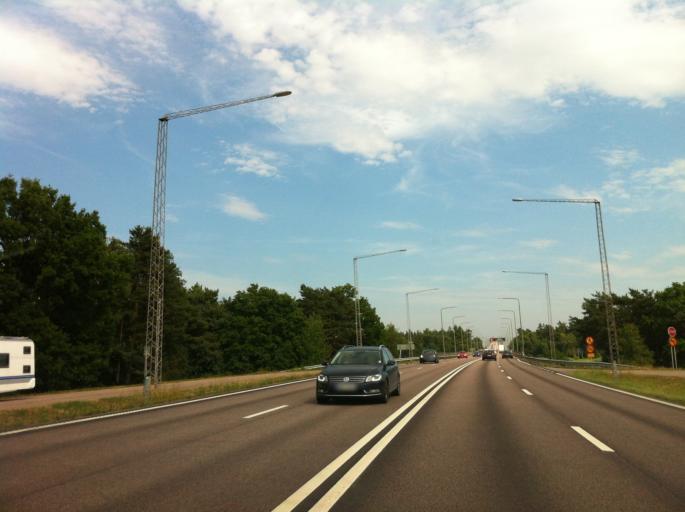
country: SE
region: Kalmar
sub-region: Kalmar Kommun
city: Kalmar
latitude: 56.6845
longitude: 16.3664
